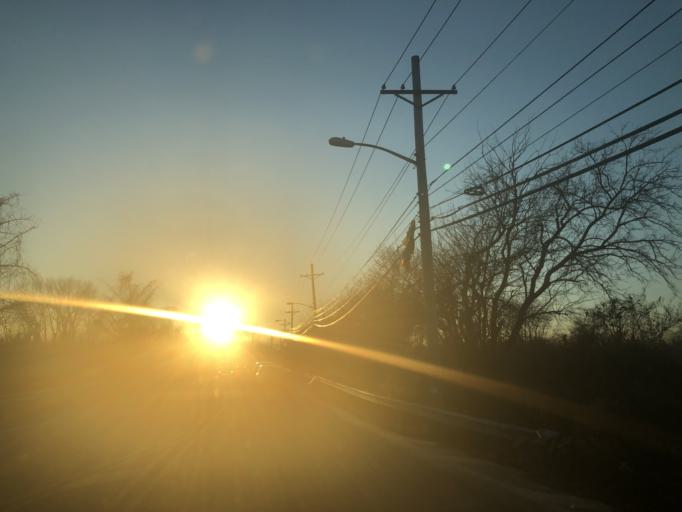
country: US
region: New Jersey
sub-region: Hudson County
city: Jersey City
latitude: 40.7059
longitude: -74.0578
